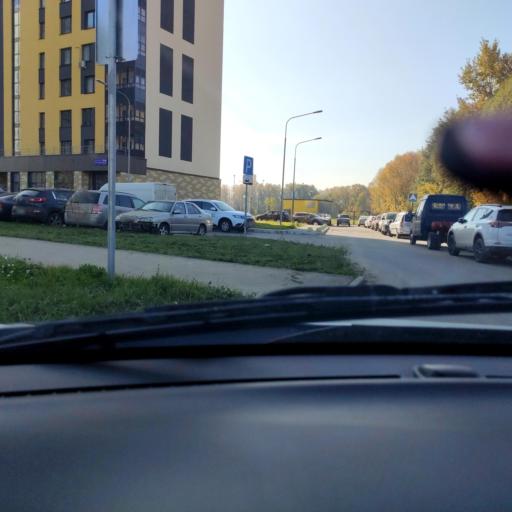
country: RU
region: Tatarstan
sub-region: Gorod Kazan'
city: Kazan
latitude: 55.8024
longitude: 49.2352
